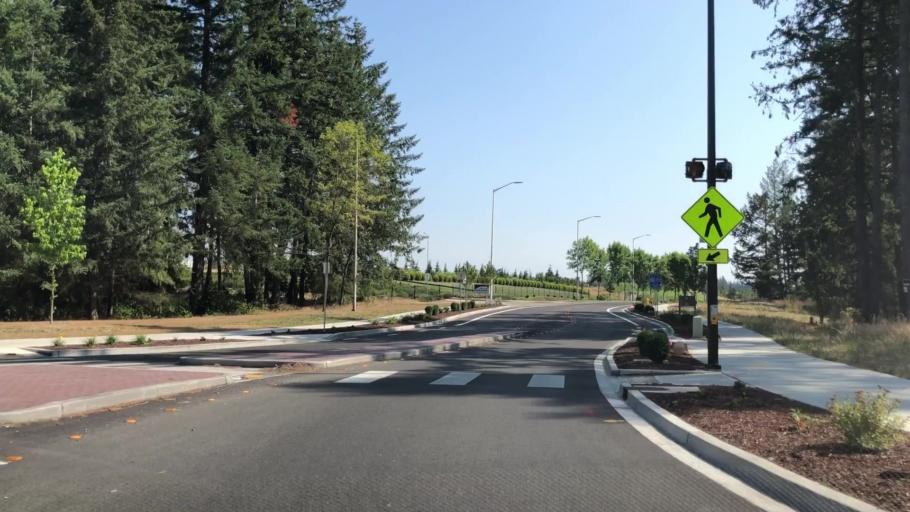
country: US
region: Washington
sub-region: Thurston County
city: Tanglewilde-Thompson Place
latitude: 47.0693
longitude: -122.7651
